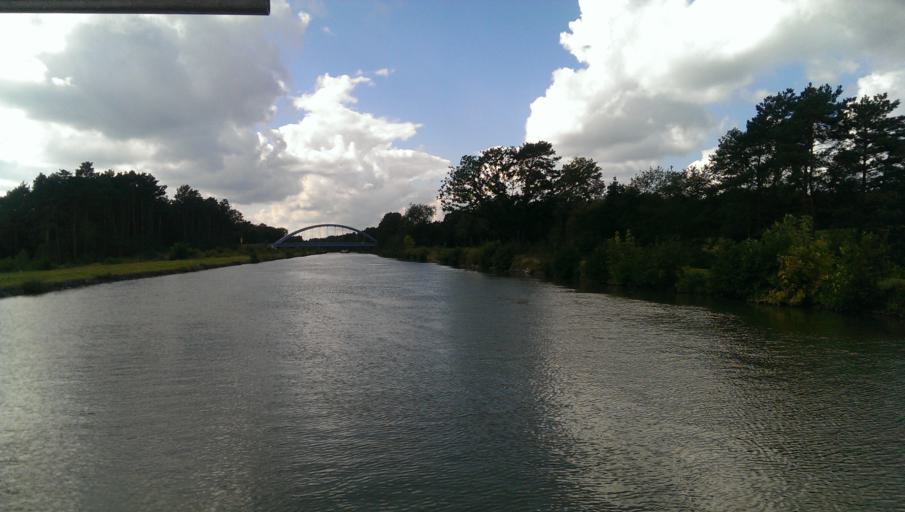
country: DE
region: Brandenburg
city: Marienwerder
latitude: 52.8557
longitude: 13.6579
